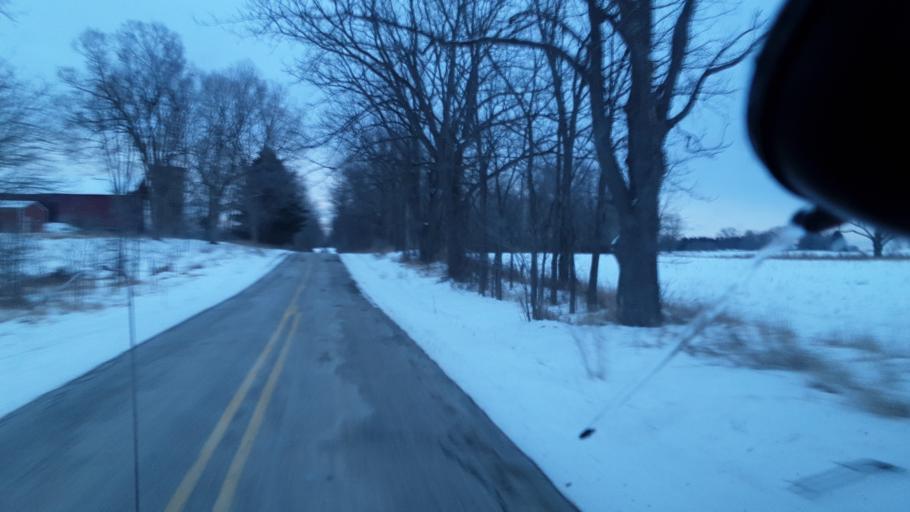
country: US
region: Michigan
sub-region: Ingham County
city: Leslie
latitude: 42.4373
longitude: -84.3409
